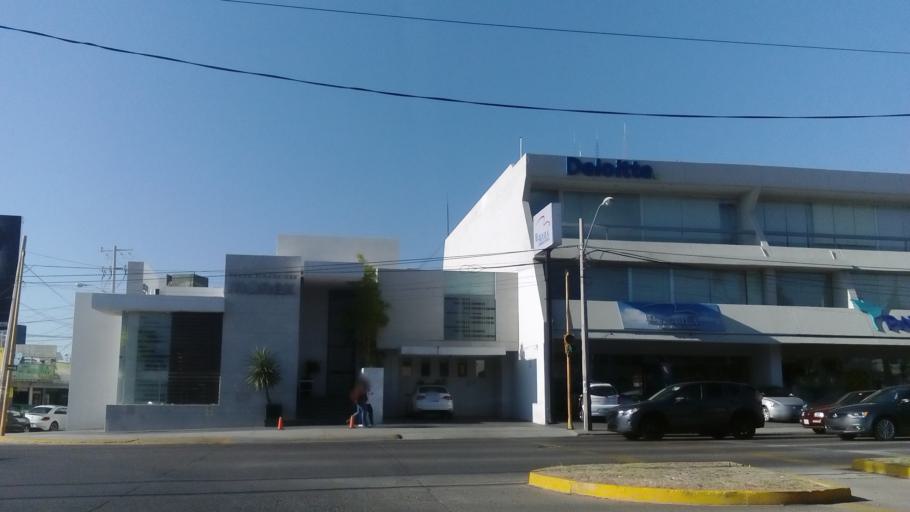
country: MX
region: Guanajuato
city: Leon
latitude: 21.1425
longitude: -101.6908
